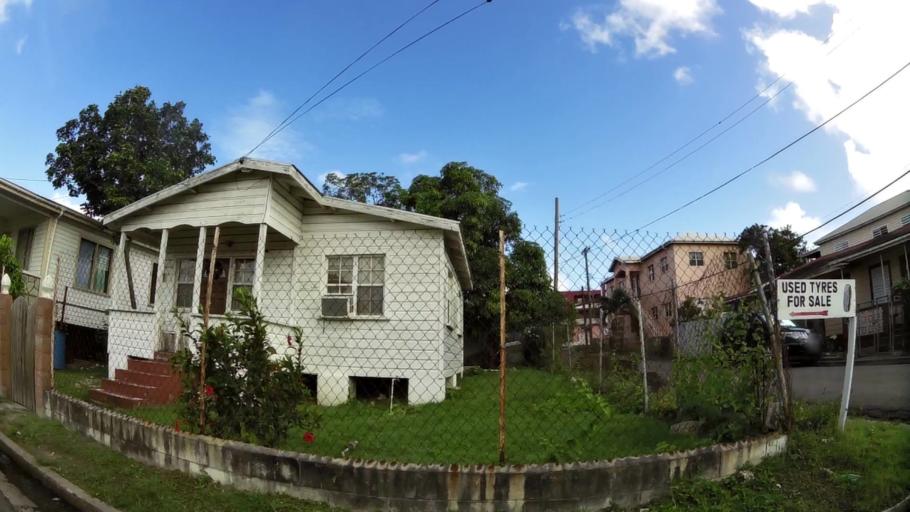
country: AG
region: Saint John
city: Saint John's
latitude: 17.1146
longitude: -61.8400
